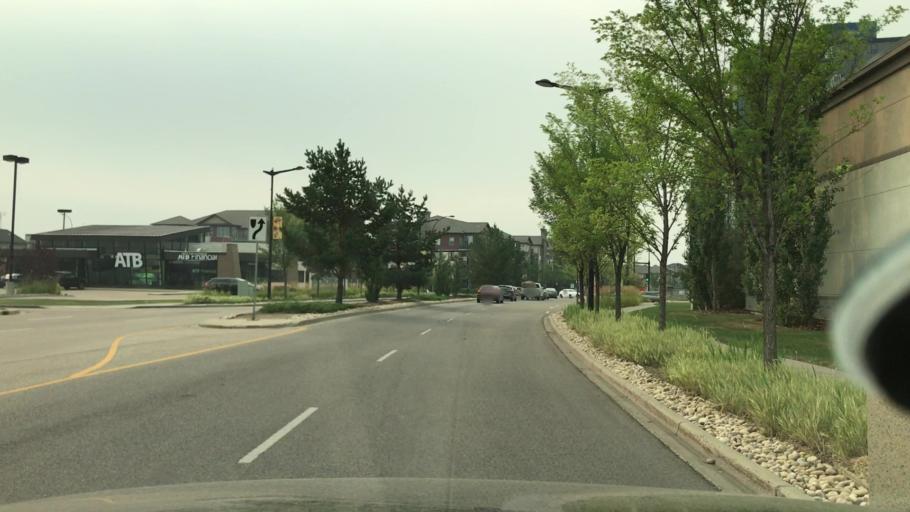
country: CA
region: Alberta
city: Devon
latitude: 53.4356
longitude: -113.5995
